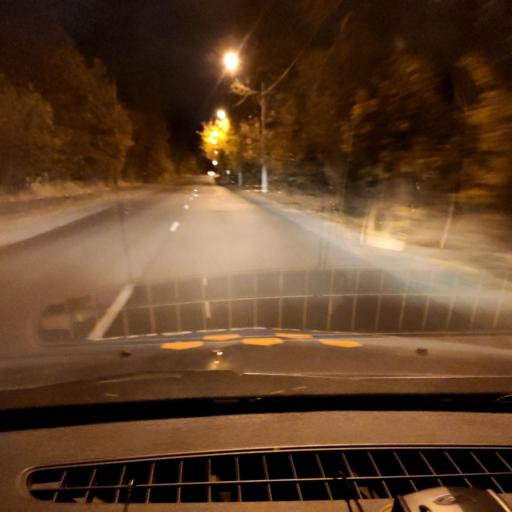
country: RU
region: Voronezj
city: Somovo
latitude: 51.7159
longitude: 39.3242
